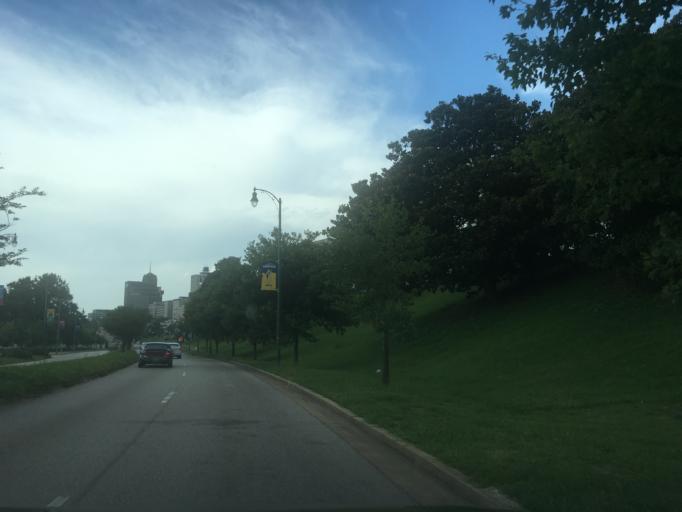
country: US
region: Tennessee
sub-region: Shelby County
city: Memphis
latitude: 35.1396
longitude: -90.0597
